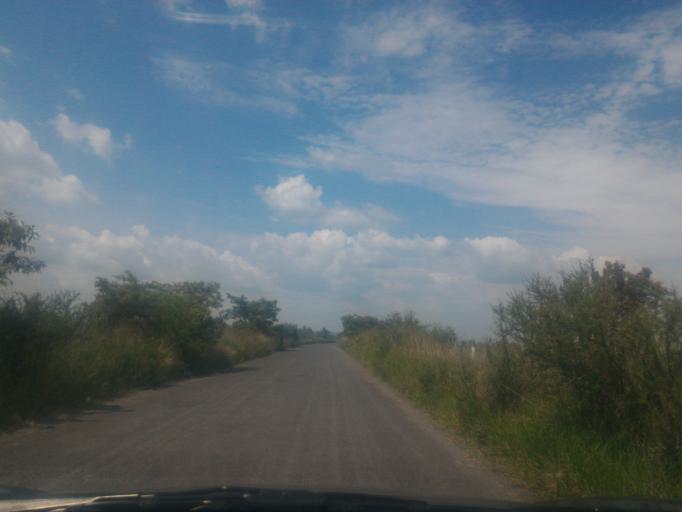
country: MX
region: Guanajuato
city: Ciudad Manuel Doblado
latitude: 20.8135
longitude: -102.0663
